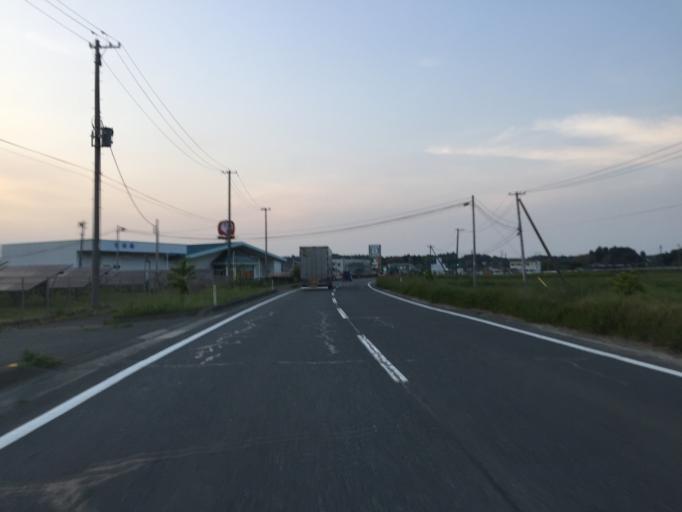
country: JP
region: Fukushima
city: Namie
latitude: 37.5604
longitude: 141.0022
